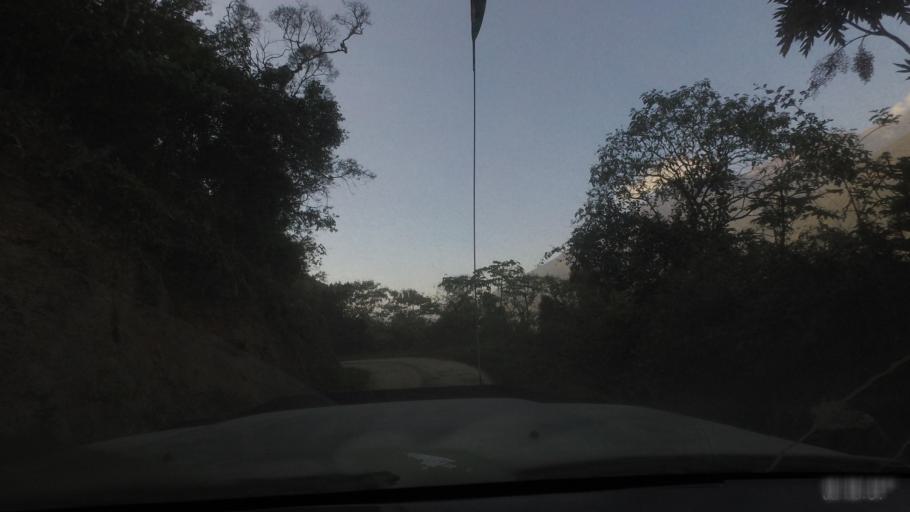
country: BO
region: La Paz
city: Quime
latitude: -16.5243
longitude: -66.7682
